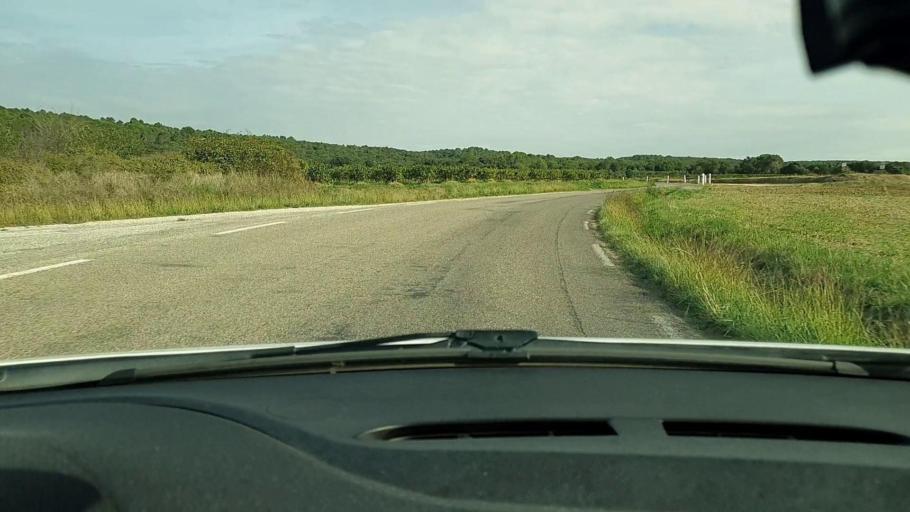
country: FR
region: Languedoc-Roussillon
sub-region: Departement du Gard
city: Saint-Quentin-la-Poterie
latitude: 44.0606
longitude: 4.4387
